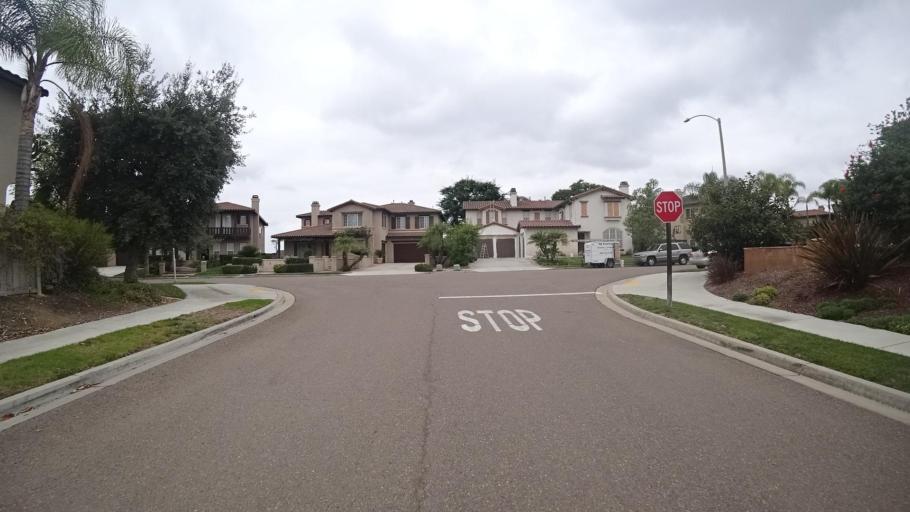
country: US
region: California
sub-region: San Diego County
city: Fairbanks Ranch
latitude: 33.0061
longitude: -117.1219
